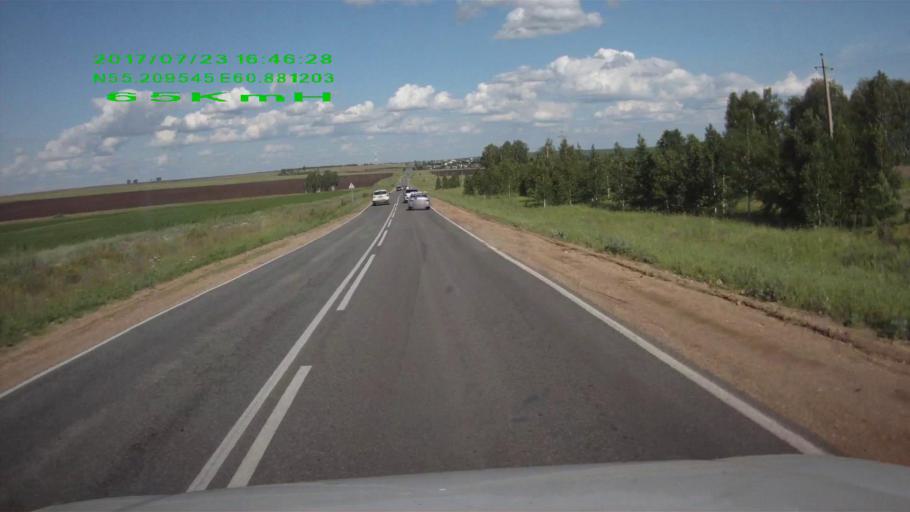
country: RU
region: Chelyabinsk
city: Argayash
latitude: 55.2088
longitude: 60.8807
